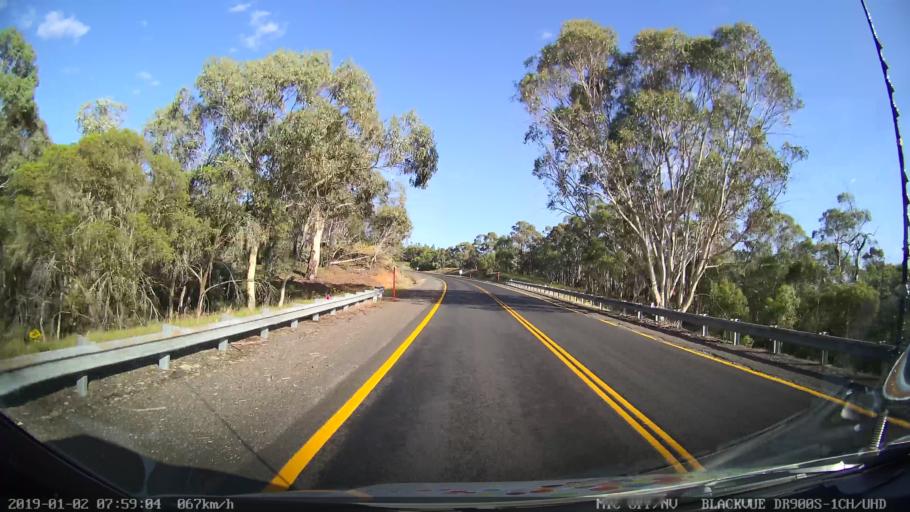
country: AU
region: New South Wales
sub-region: Tumut Shire
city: Tumut
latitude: -35.6476
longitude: 148.4618
